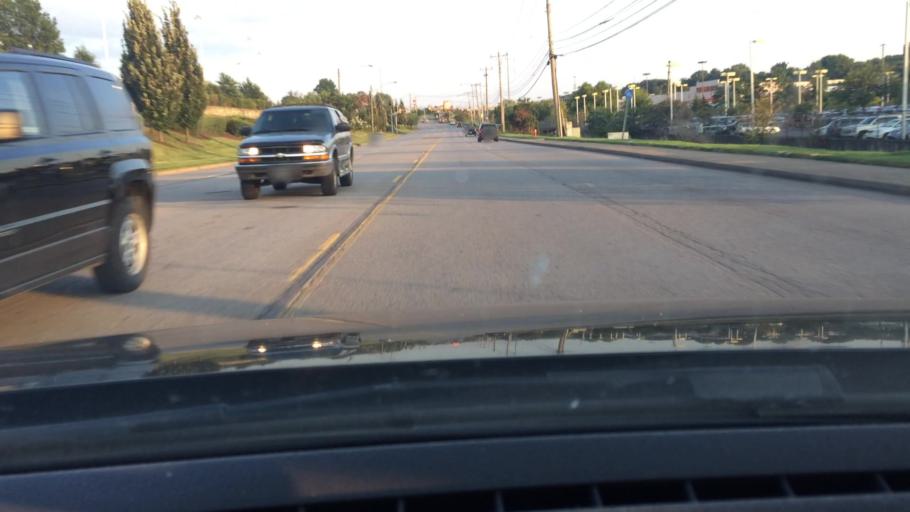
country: US
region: Tennessee
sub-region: Davidson County
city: Oak Hill
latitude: 36.1103
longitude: -86.7669
